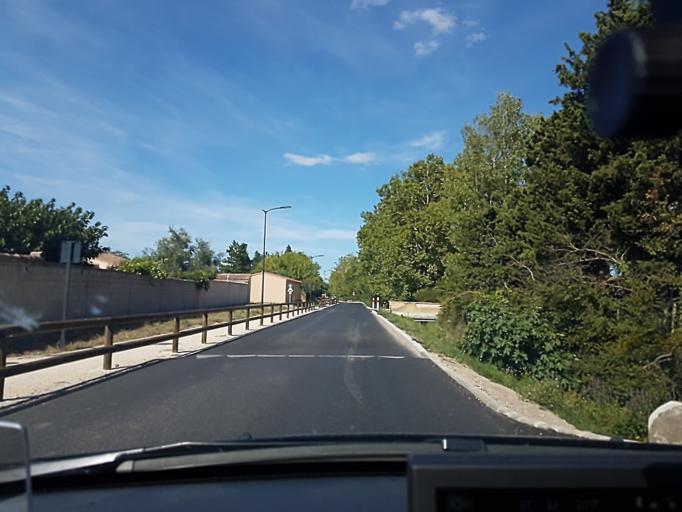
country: FR
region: Provence-Alpes-Cote d'Azur
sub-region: Departement du Vaucluse
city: Caumont-sur-Durance
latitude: 43.8967
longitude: 4.9507
